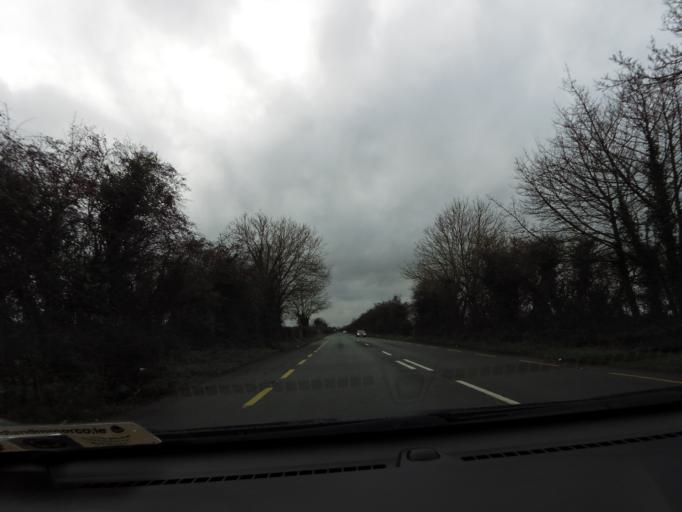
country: IE
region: Leinster
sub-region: Kilkenny
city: Ballyragget
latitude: 52.7716
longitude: -7.3316
